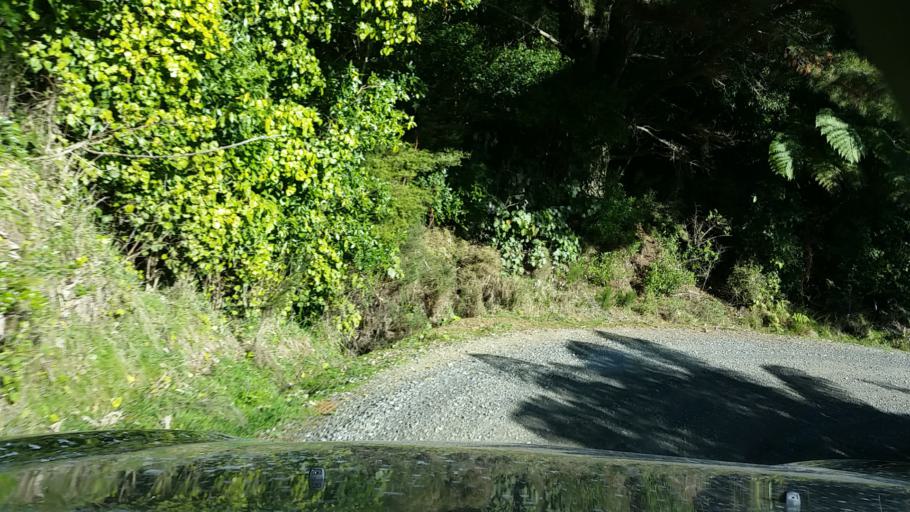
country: NZ
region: Marlborough
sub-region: Marlborough District
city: Picton
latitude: -41.1338
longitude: 174.0432
